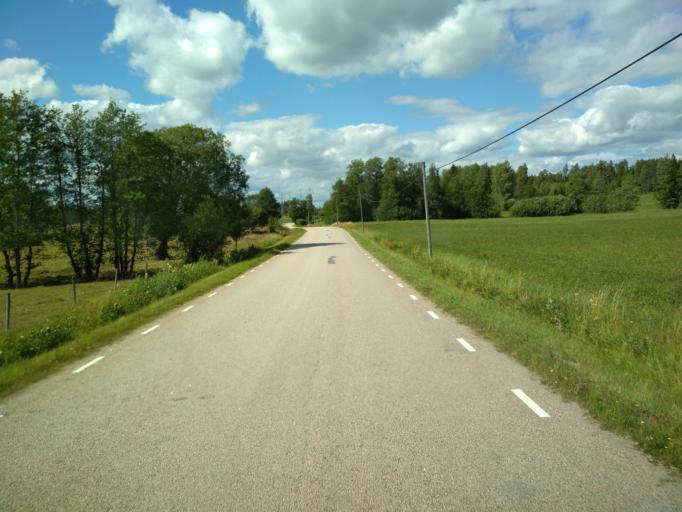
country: SE
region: Uppsala
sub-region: Enkopings Kommun
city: Orsundsbro
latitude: 59.7807
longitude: 17.2101
